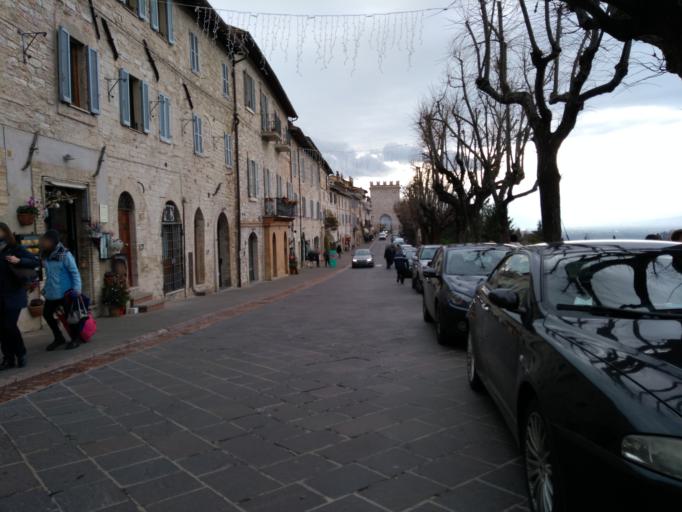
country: IT
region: Umbria
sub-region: Provincia di Perugia
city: Assisi
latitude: 43.0685
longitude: 12.6179
